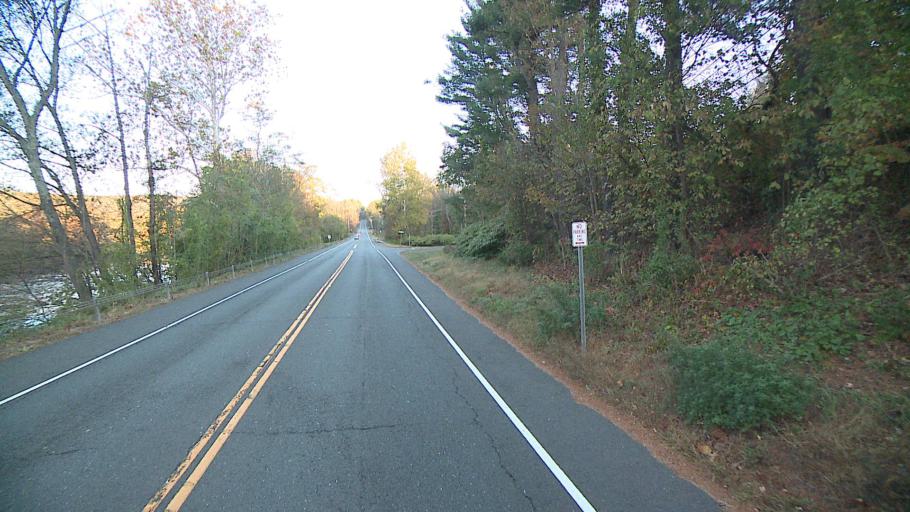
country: US
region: Connecticut
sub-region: Hartford County
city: Collinsville
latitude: 41.8422
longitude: -72.9381
